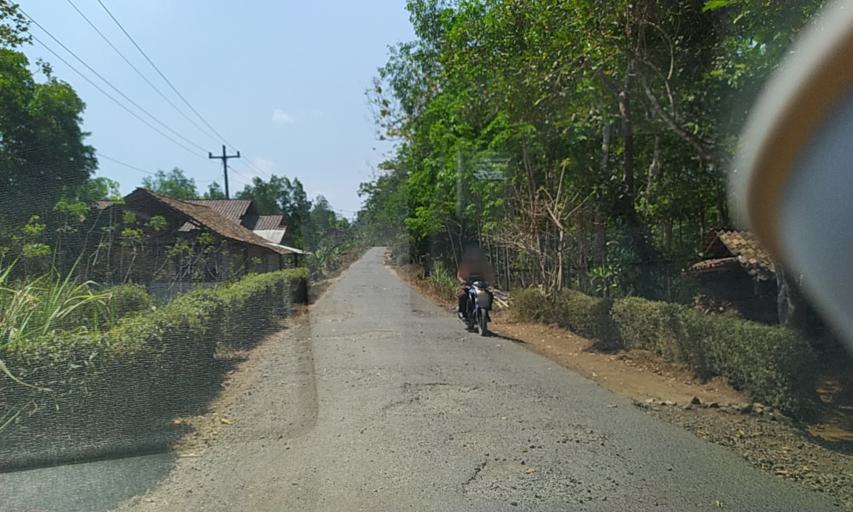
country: ID
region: Central Java
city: Karanggintung
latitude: -7.4507
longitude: 108.8555
